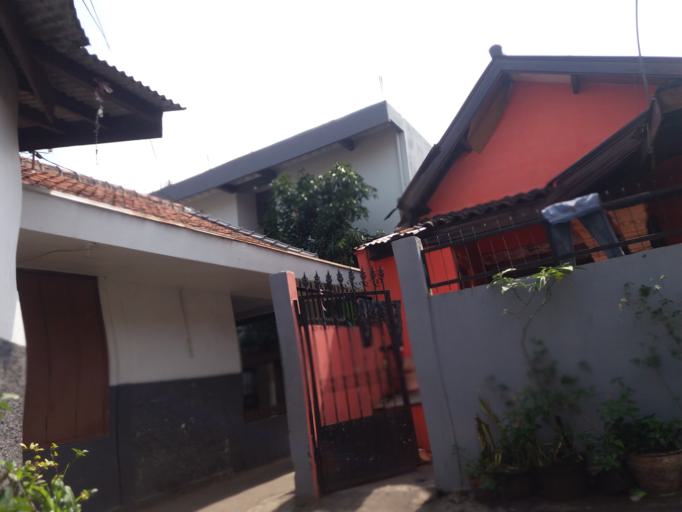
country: ID
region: West Java
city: Bandung
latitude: -6.9218
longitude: 107.6457
